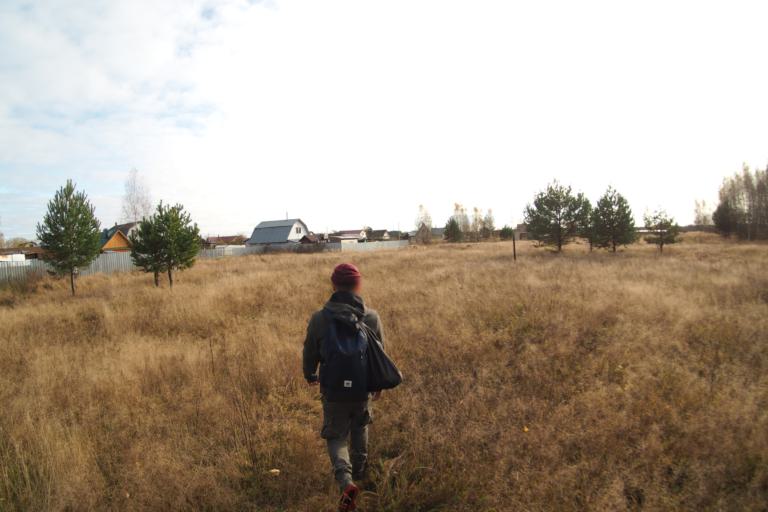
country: RU
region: Moskovskaya
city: Davydovo
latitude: 55.5590
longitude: 38.8043
